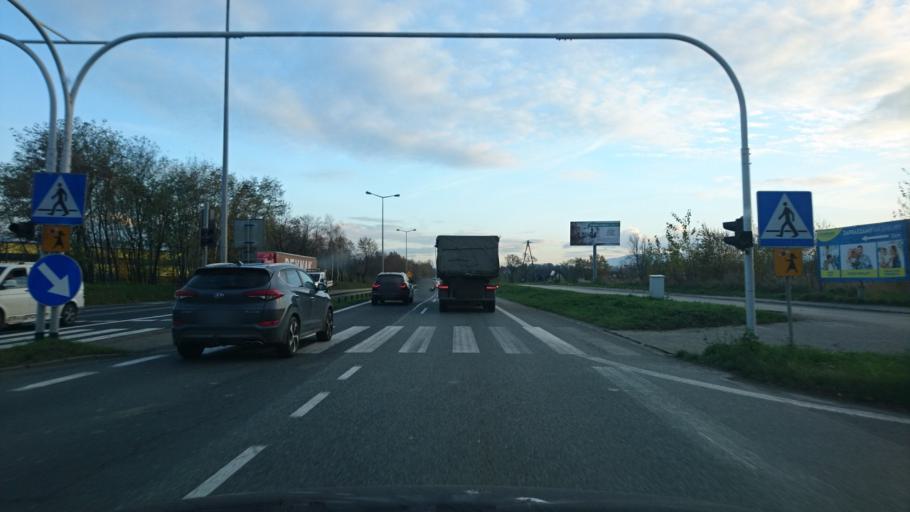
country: PL
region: Silesian Voivodeship
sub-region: Powiat bielski
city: Czechowice-Dziedzice
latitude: 49.8923
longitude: 18.9934
